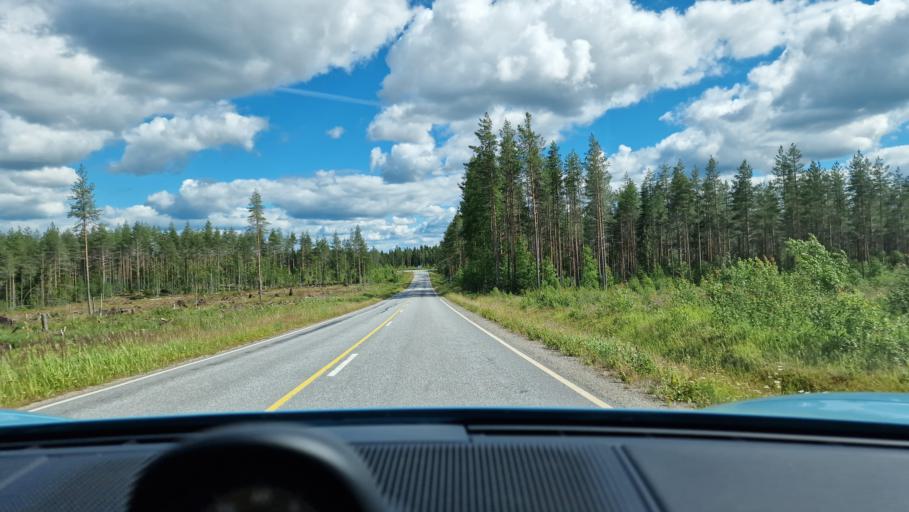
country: FI
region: Central Finland
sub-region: Saarijaervi-Viitasaari
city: Pylkoenmaeki
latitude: 62.6599
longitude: 24.5648
